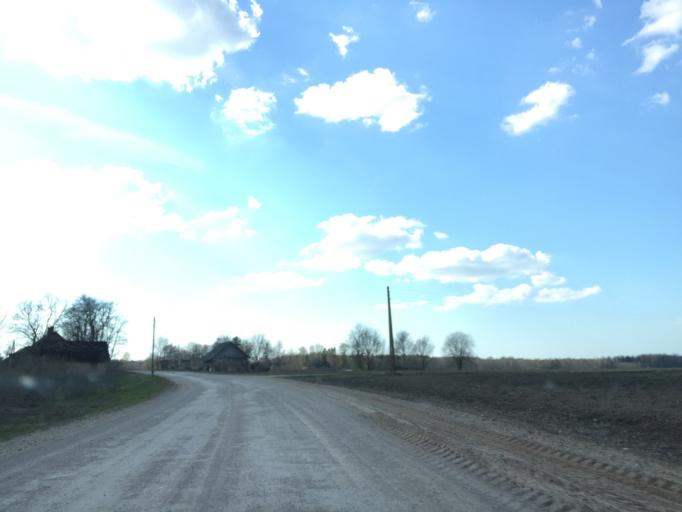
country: LV
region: Krimulda
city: Ragana
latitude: 57.3399
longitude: 24.6249
